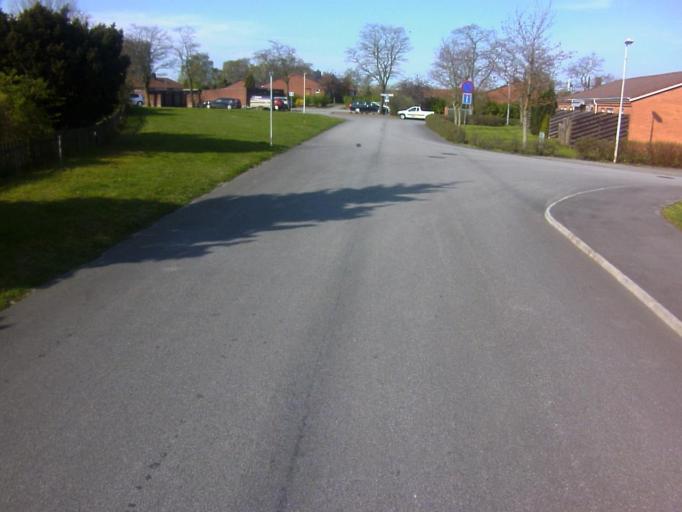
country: SE
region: Skane
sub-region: Kavlinge Kommun
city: Loddekopinge
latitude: 55.7577
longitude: 13.0127
